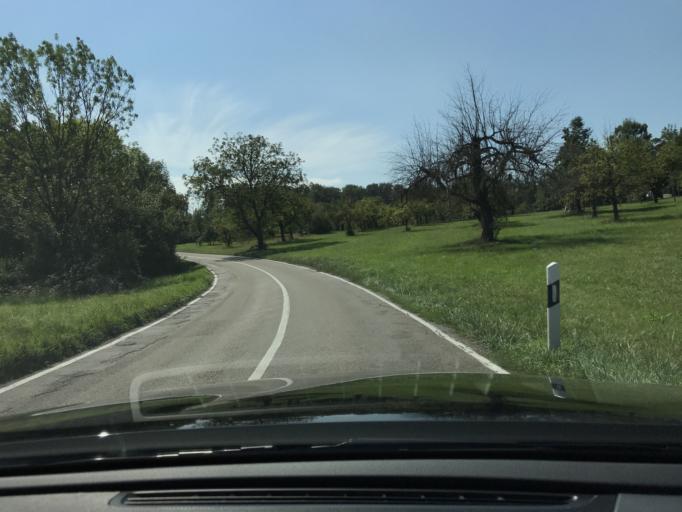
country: DE
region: Baden-Wuerttemberg
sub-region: Regierungsbezirk Stuttgart
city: Affalterbach
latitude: 48.9159
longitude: 9.3155
